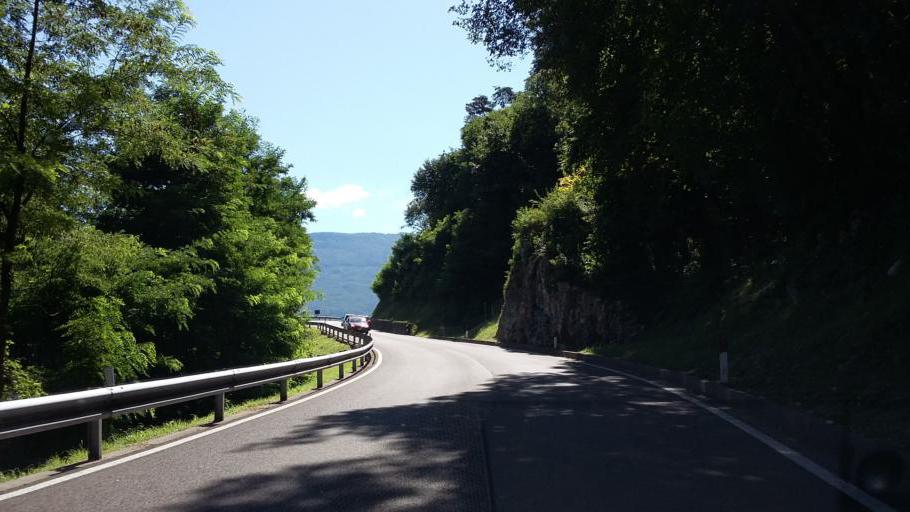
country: IT
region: Trentino-Alto Adige
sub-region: Provincia di Trento
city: Mori
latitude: 45.8473
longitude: 10.9711
